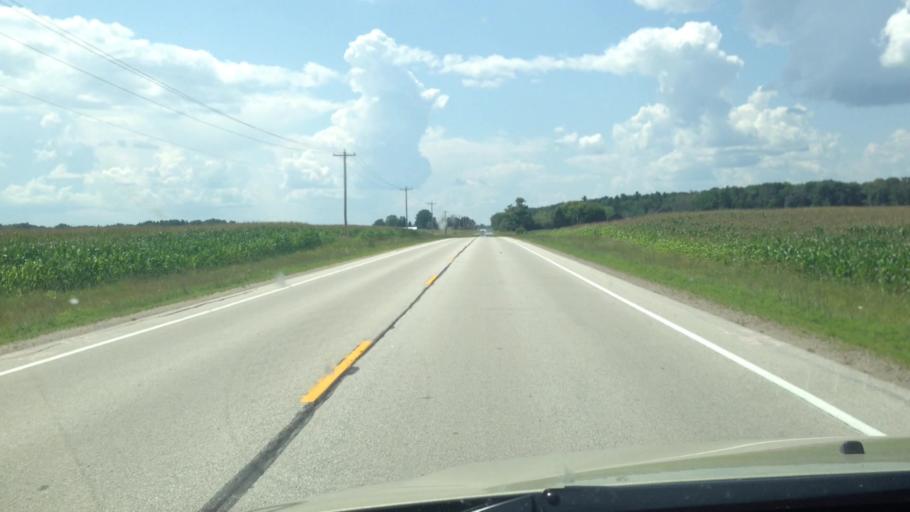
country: US
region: Wisconsin
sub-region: Brown County
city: Pulaski
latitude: 44.6588
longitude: -88.1874
